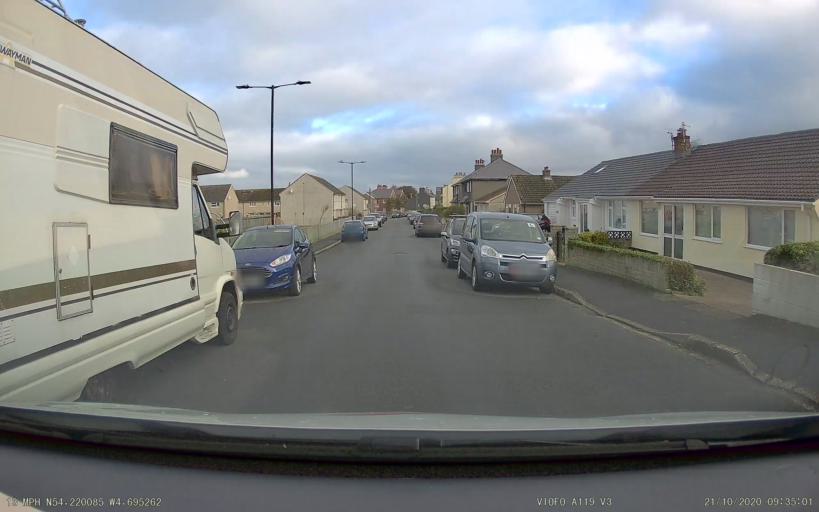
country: IM
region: Port Erin
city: Port Erin
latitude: 54.2202
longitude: -4.6952
